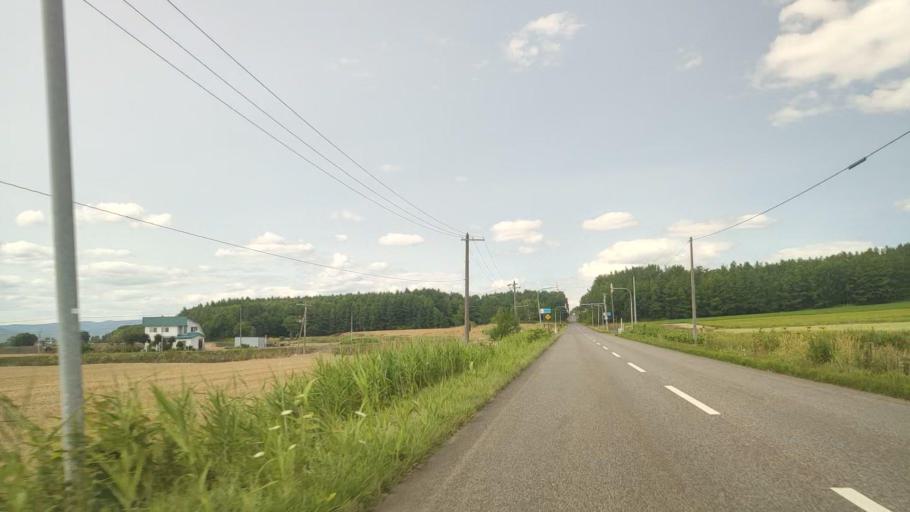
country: JP
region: Hokkaido
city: Nayoro
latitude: 44.2400
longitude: 142.4157
